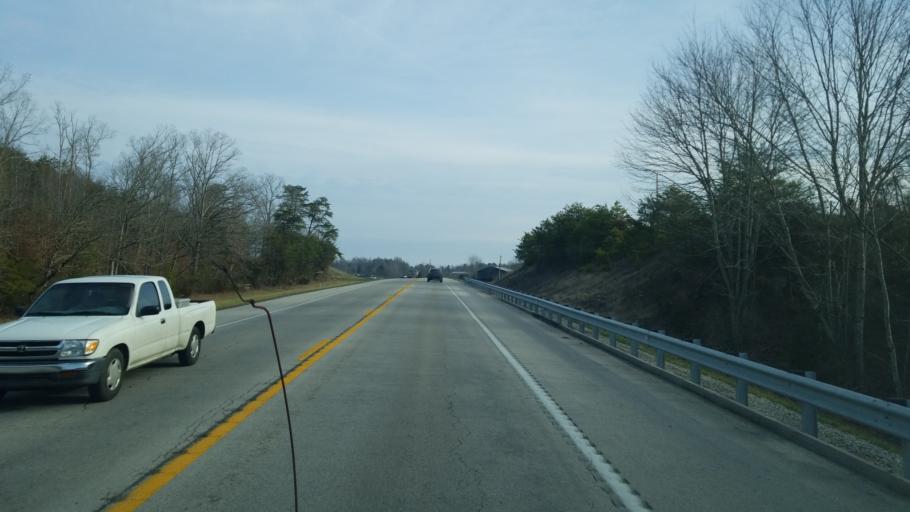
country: US
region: Kentucky
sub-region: Russell County
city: Russell Springs
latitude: 37.1648
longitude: -85.0099
